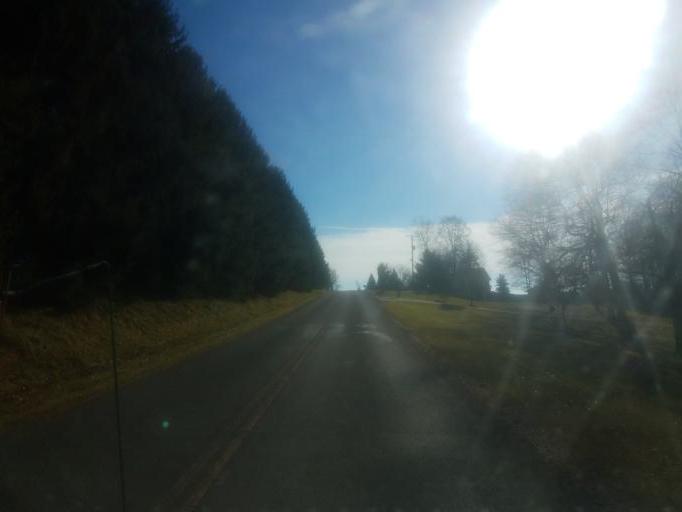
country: US
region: Ohio
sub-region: Richland County
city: Lexington
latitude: 40.7149
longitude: -82.5991
